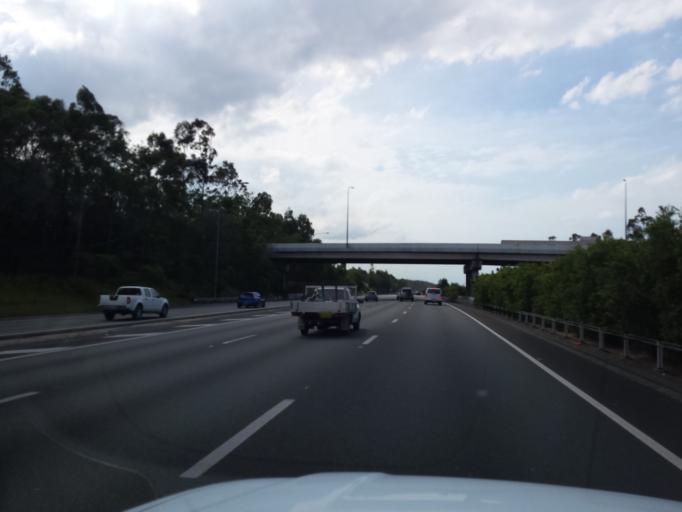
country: AU
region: Queensland
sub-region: Gold Coast
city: Nerang
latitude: -27.9520
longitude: 153.3429
